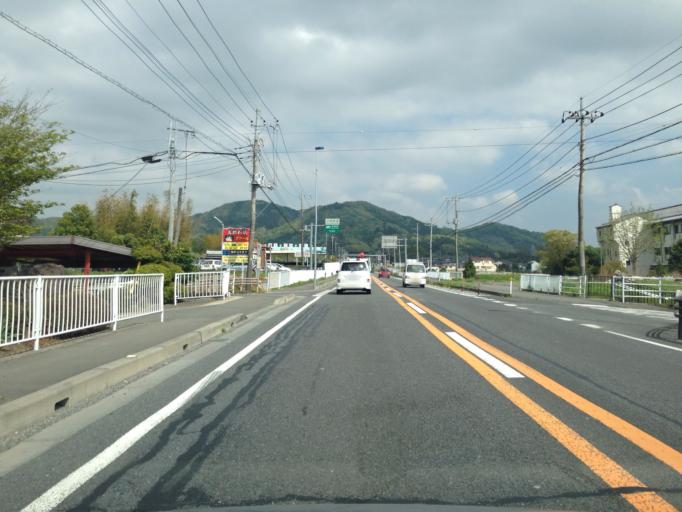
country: JP
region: Ibaraki
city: Iwase
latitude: 36.3579
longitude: 140.1460
